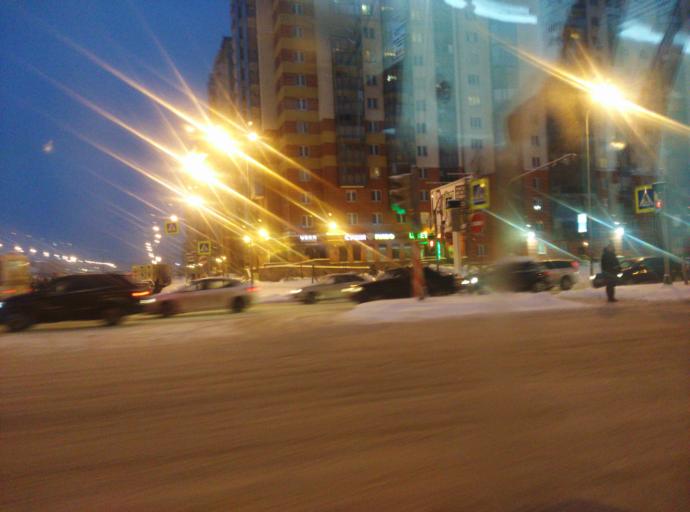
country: RU
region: St.-Petersburg
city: Komendantsky aerodrom
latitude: 60.0209
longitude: 30.2642
